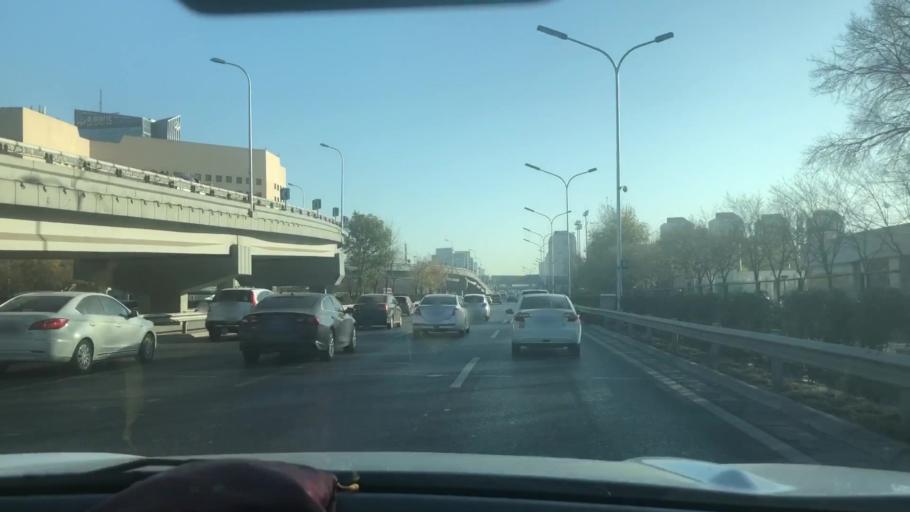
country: CN
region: Beijing
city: Datun
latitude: 39.9867
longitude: 116.3935
